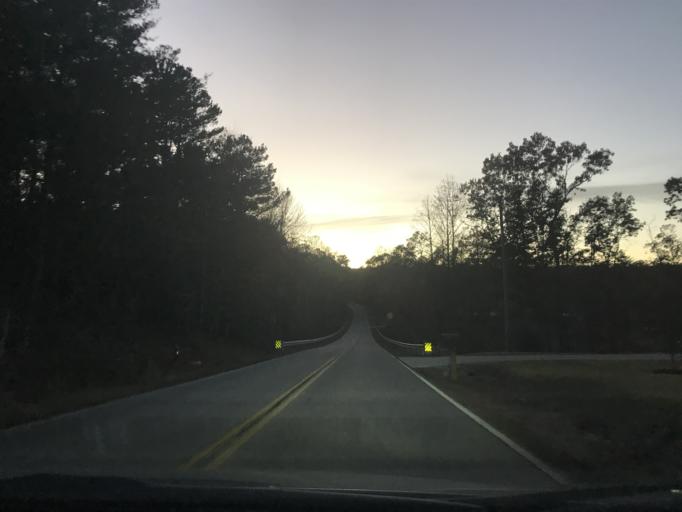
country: US
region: South Carolina
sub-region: Spartanburg County
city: Mayo
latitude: 35.0878
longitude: -81.8918
